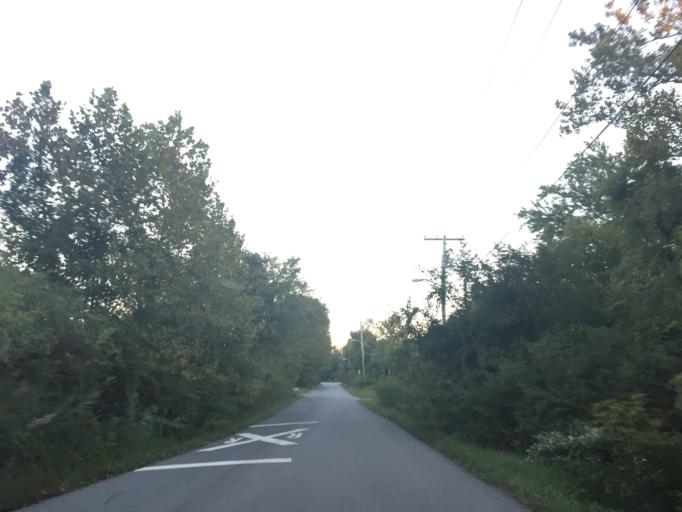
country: US
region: Maryland
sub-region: Baltimore County
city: Kingsville
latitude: 39.4136
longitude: -76.3881
